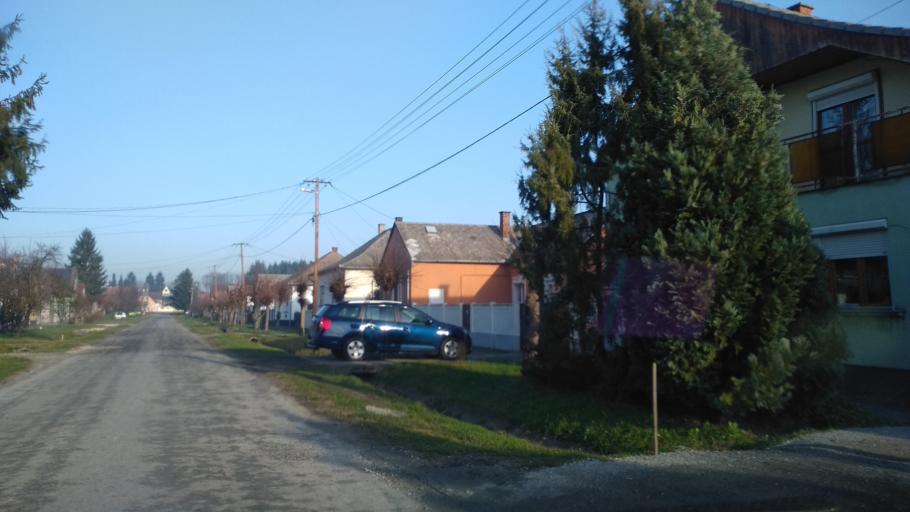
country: HU
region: Somogy
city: Barcs
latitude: 45.9637
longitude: 17.4745
